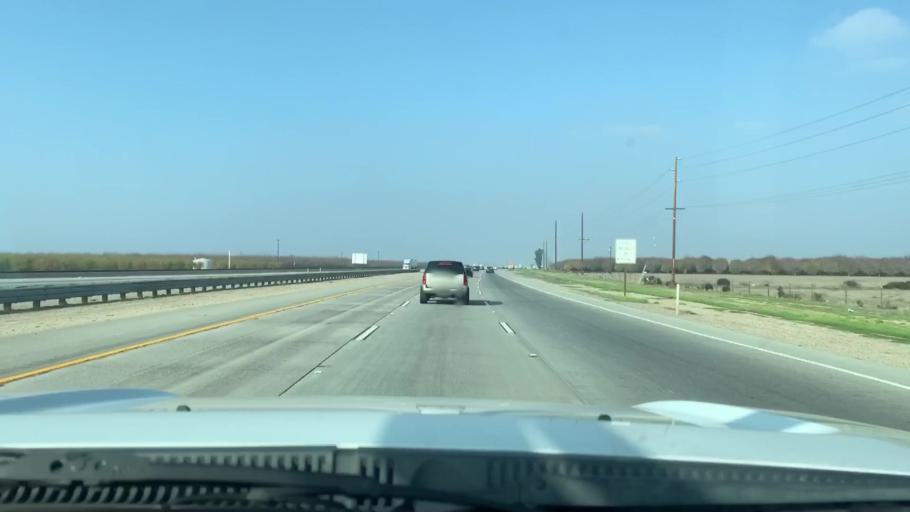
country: US
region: California
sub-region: Kern County
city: Shafter
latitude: 35.5343
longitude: -119.1919
